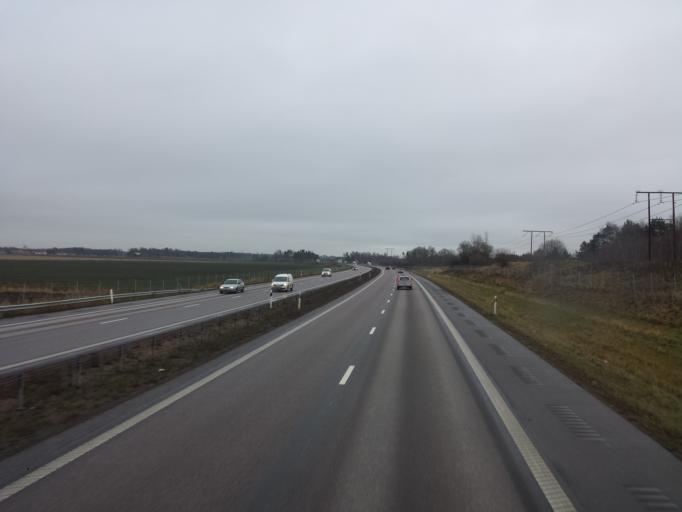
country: SE
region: OEstergoetland
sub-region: Linkopings Kommun
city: Ekangen
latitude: 58.4362
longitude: 15.6952
